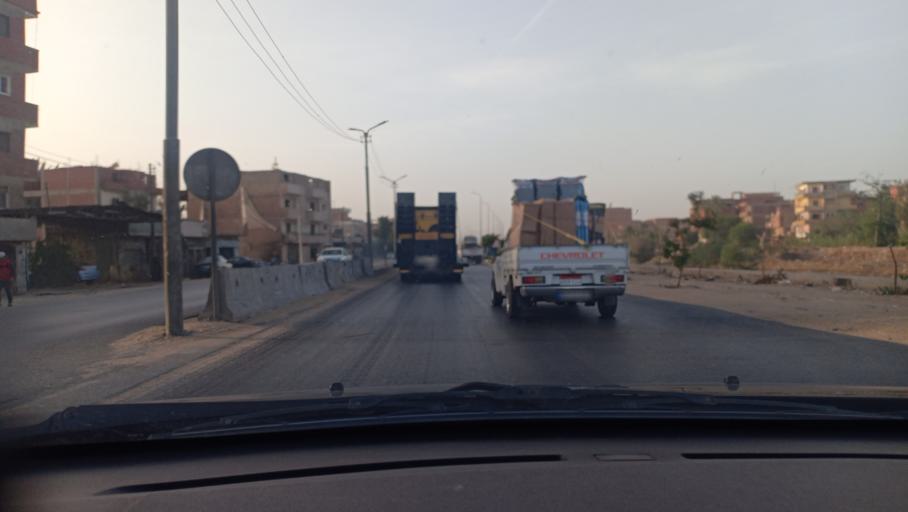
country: EG
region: Muhafazat al Minufiyah
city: Quwaysina
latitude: 30.5431
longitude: 31.2693
